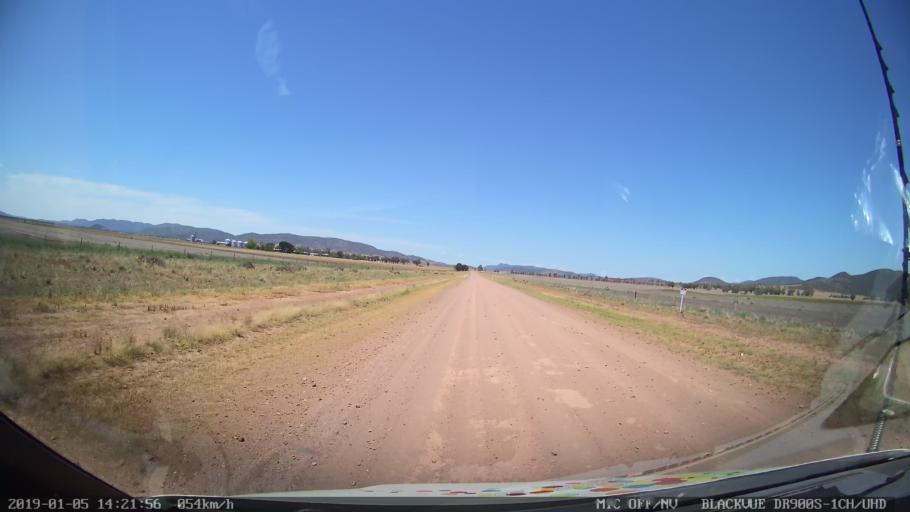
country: AU
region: New South Wales
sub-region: Liverpool Plains
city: Quirindi
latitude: -31.2456
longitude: 150.5177
